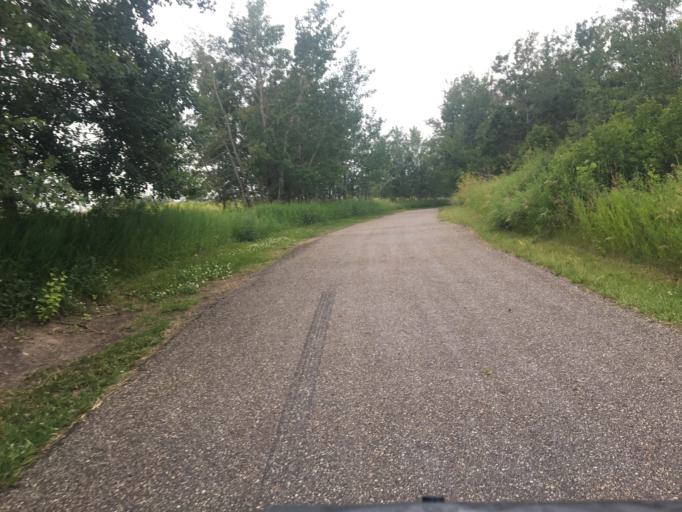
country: CA
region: Alberta
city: Grande Prairie
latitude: 55.1609
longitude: -118.8048
